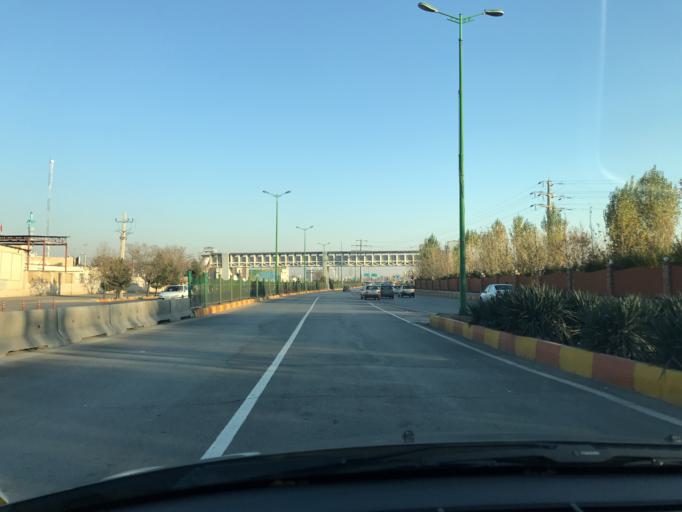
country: IR
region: Qazvin
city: Qazvin
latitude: 36.2878
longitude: 50.0091
